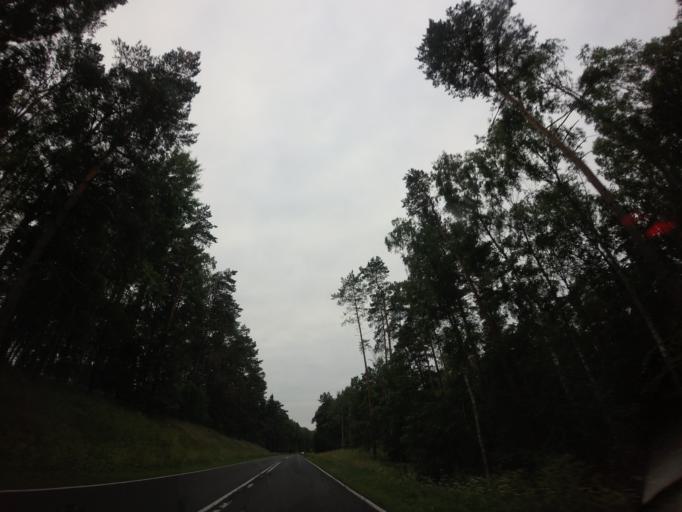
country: PL
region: West Pomeranian Voivodeship
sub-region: Powiat drawski
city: Kalisz Pomorski
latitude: 53.2908
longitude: 15.9516
